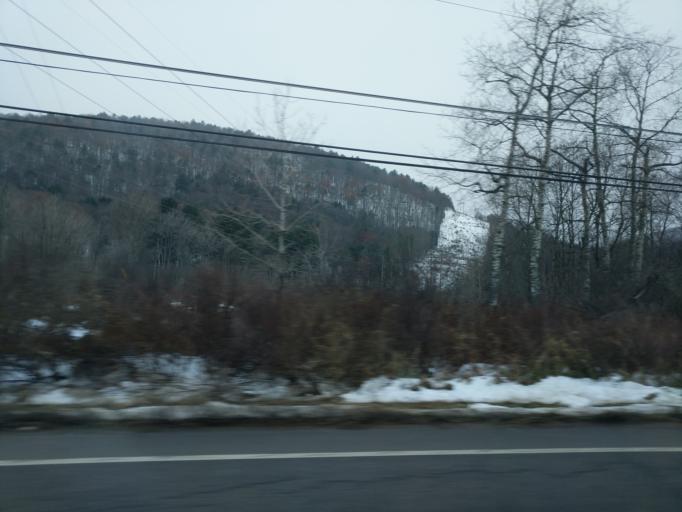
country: US
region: Pennsylvania
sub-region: Tioga County
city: Wellsboro
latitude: 41.8200
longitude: -77.2892
